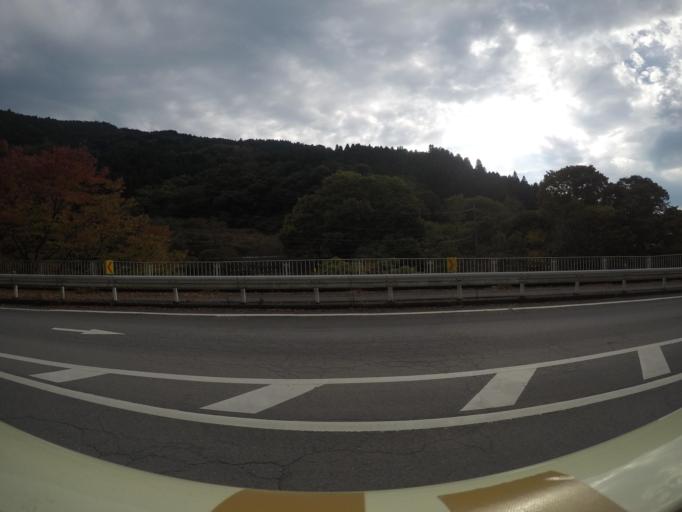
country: JP
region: Gunma
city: Tomioka
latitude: 36.1160
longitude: 138.9328
